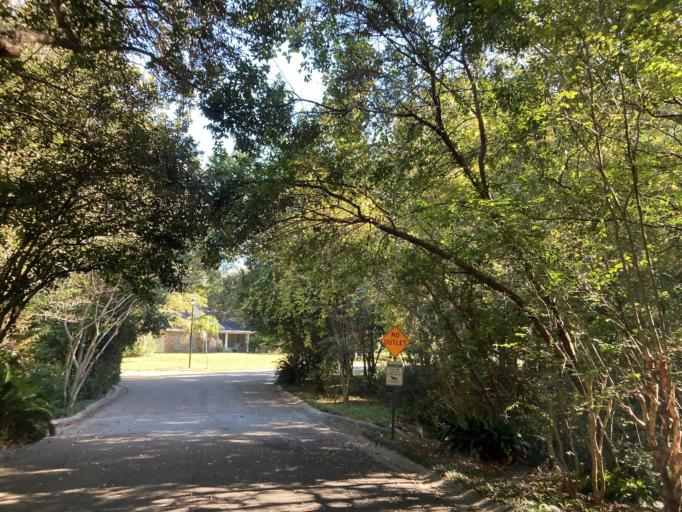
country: US
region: Mississippi
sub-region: Jackson County
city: Ocean Springs
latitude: 30.4153
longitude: -88.8412
